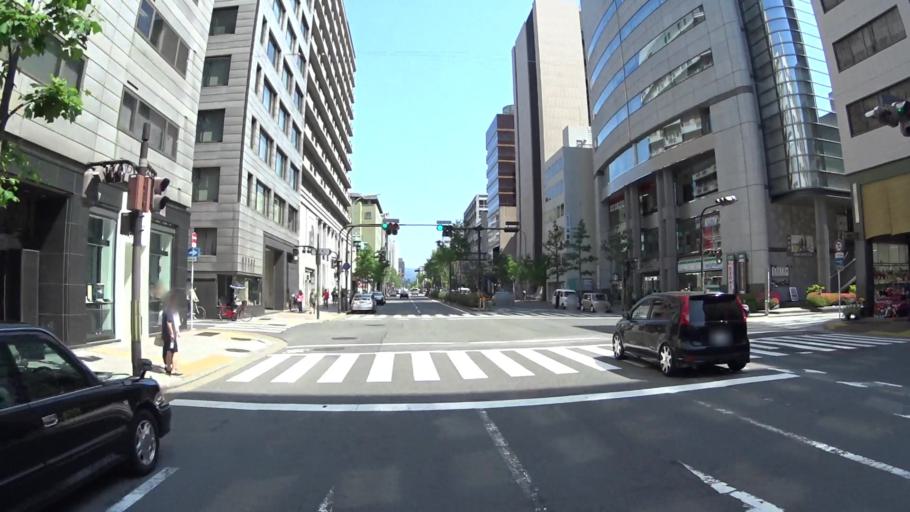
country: JP
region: Kyoto
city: Kyoto
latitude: 35.0070
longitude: 135.7597
